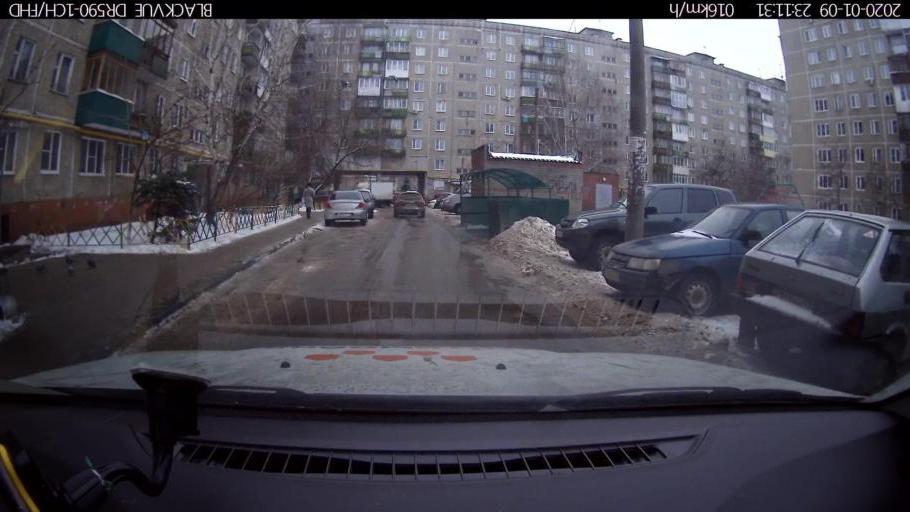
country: RU
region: Nizjnij Novgorod
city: Gorbatovka
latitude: 56.3649
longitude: 43.8137
